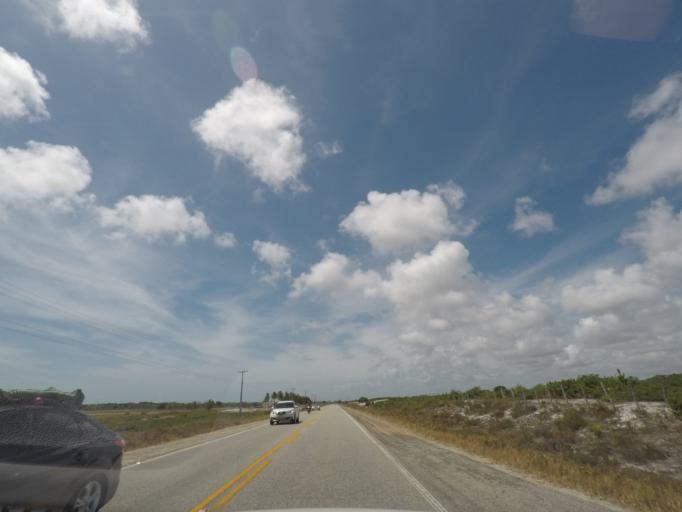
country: BR
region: Sergipe
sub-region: Sao Cristovao
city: Sao Cristovao
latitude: -11.1837
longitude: -37.2171
